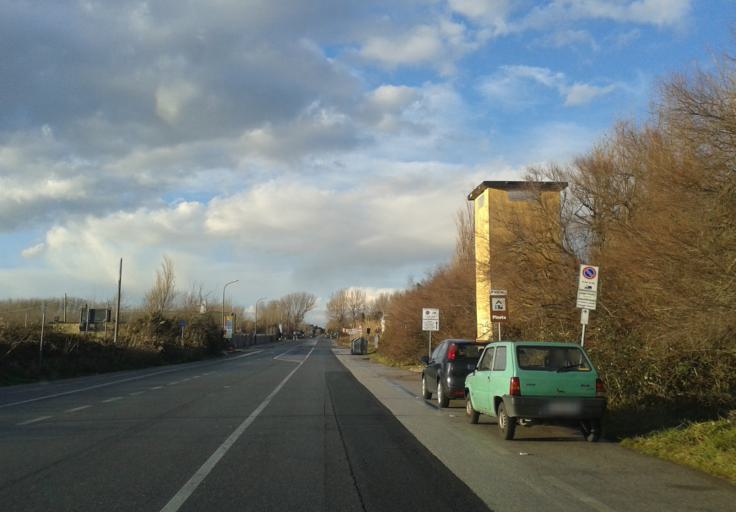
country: IT
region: Tuscany
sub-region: Province of Pisa
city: Marina di Pisa-Tirrenia-Calambrone
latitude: 43.5849
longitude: 10.3010
